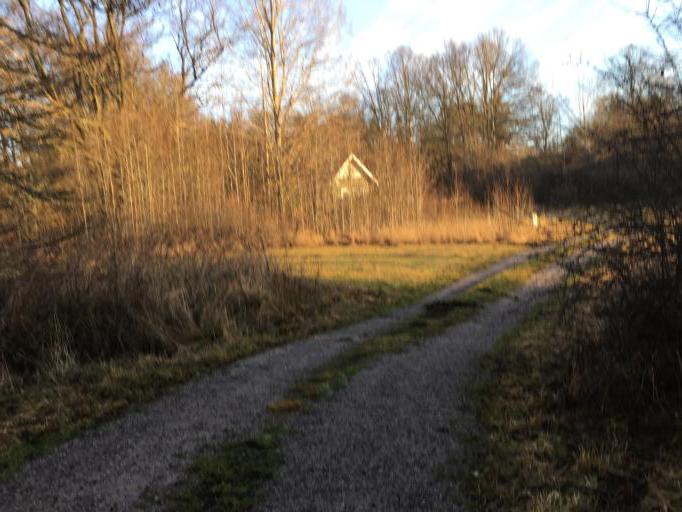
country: SE
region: Kalmar
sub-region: Vasterviks Kommun
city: Vaestervik
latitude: 57.6280
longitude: 16.5290
